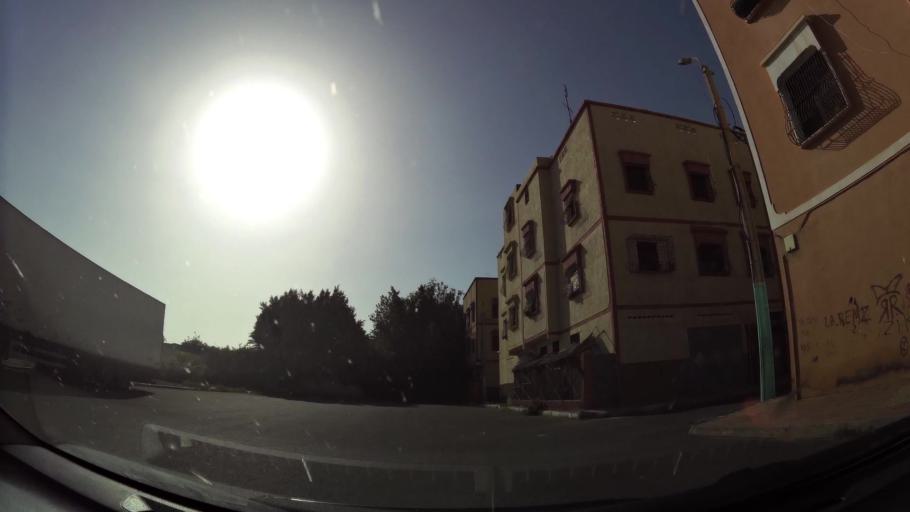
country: MA
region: Souss-Massa-Draa
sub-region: Inezgane-Ait Mellou
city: Inezgane
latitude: 30.3702
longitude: -9.5304
